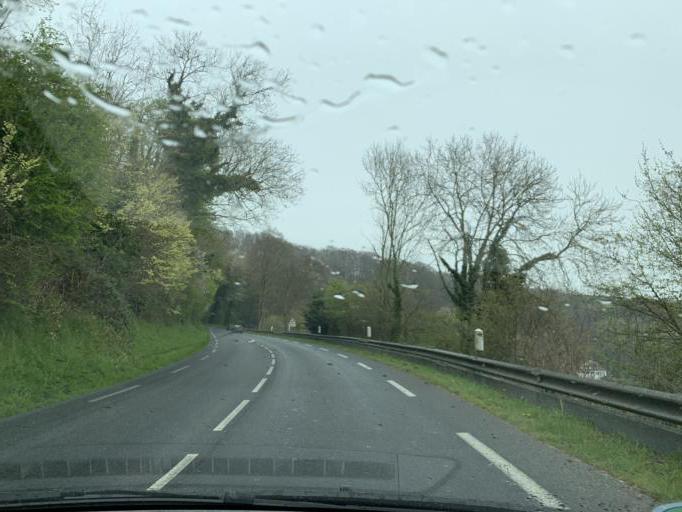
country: FR
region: Haute-Normandie
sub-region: Departement de la Seine-Maritime
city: Cany-Barville
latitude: 49.7874
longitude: 0.6434
